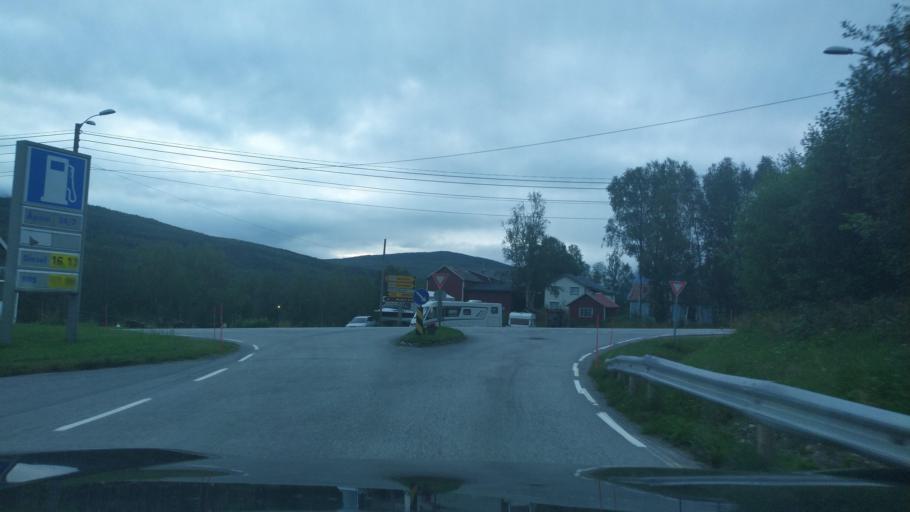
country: NO
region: Troms
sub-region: Lavangen
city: Tennevoll
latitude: 68.7491
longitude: 17.8167
